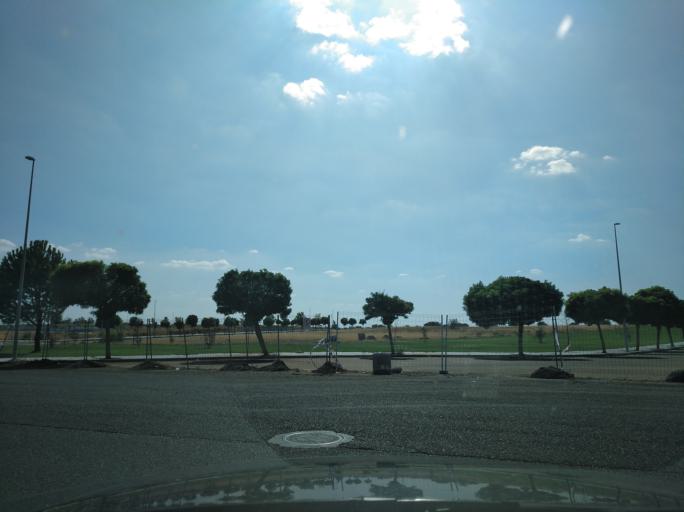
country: ES
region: Extremadura
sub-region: Provincia de Badajoz
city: Badajoz
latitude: 38.8948
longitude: -6.9997
